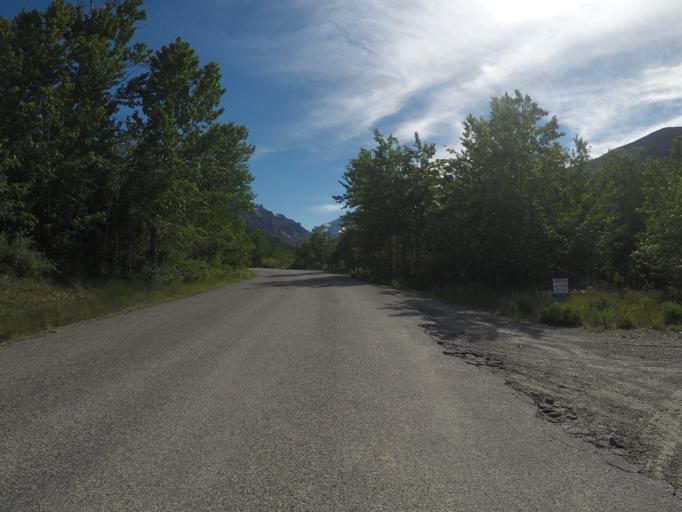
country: US
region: Montana
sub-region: Stillwater County
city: Absarokee
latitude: 45.2541
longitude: -109.5713
